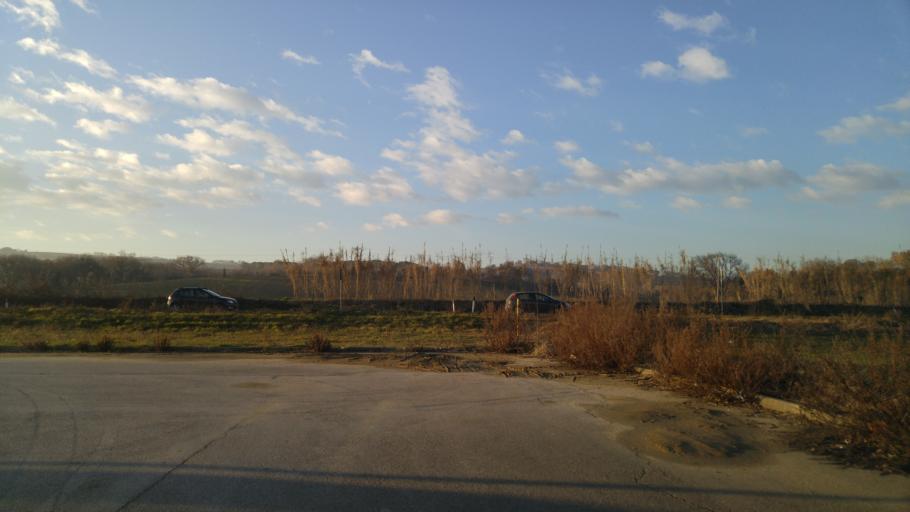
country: IT
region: The Marches
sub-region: Provincia di Ancona
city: Monterado
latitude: 43.7131
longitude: 13.0788
